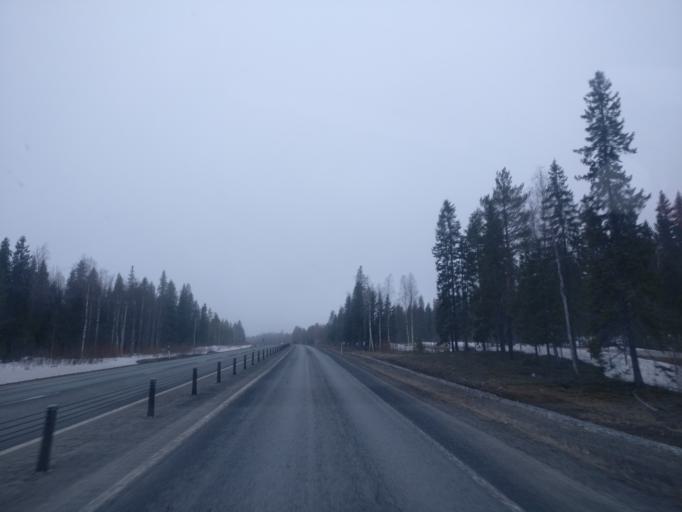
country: FI
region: Lapland
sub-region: Kemi-Tornio
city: Simo
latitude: 65.6668
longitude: 24.9788
